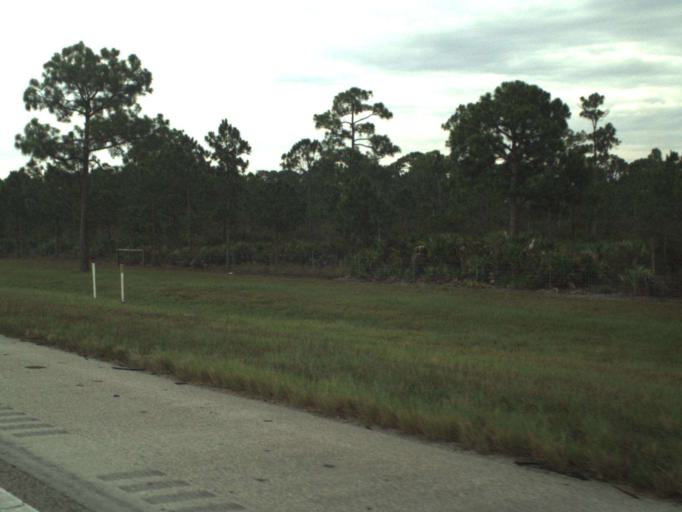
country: US
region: Florida
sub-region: Martin County
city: Palm City
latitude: 27.1269
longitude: -80.2917
